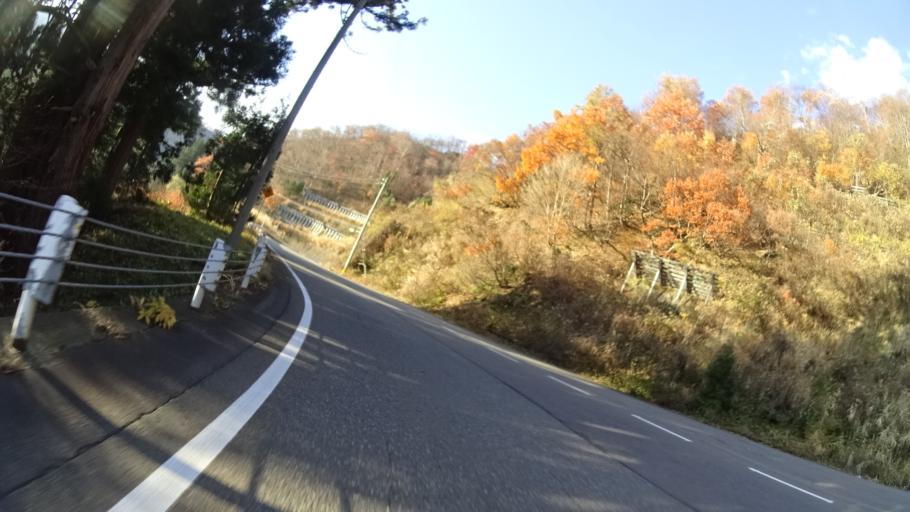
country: JP
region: Niigata
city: Shiozawa
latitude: 36.9855
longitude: 138.7479
